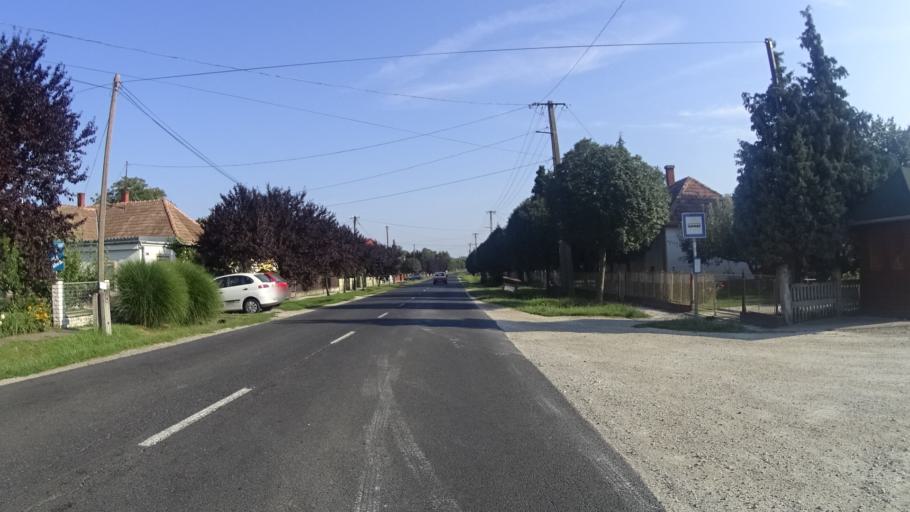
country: HU
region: Zala
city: Sarmellek
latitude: 46.6955
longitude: 17.1674
